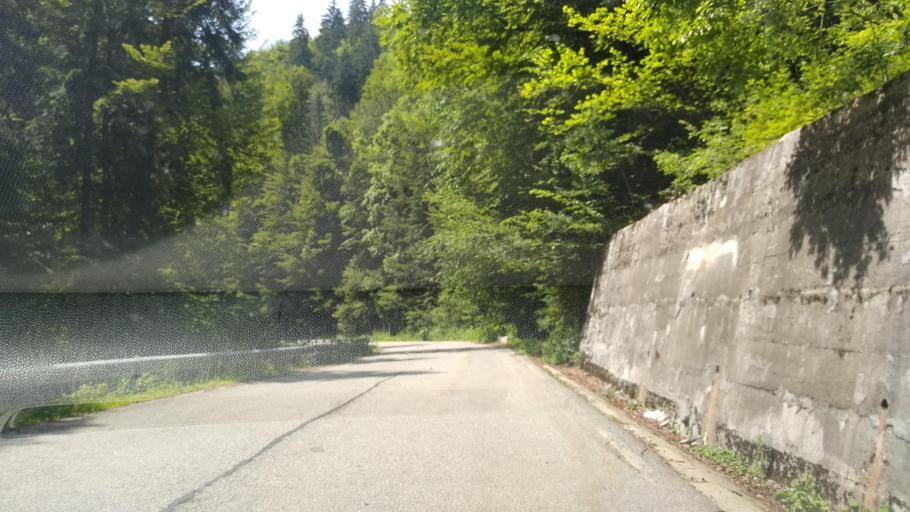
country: RO
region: Gorj
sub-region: Comuna Runcu
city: Valea Mare
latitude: 45.2735
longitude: 22.9543
